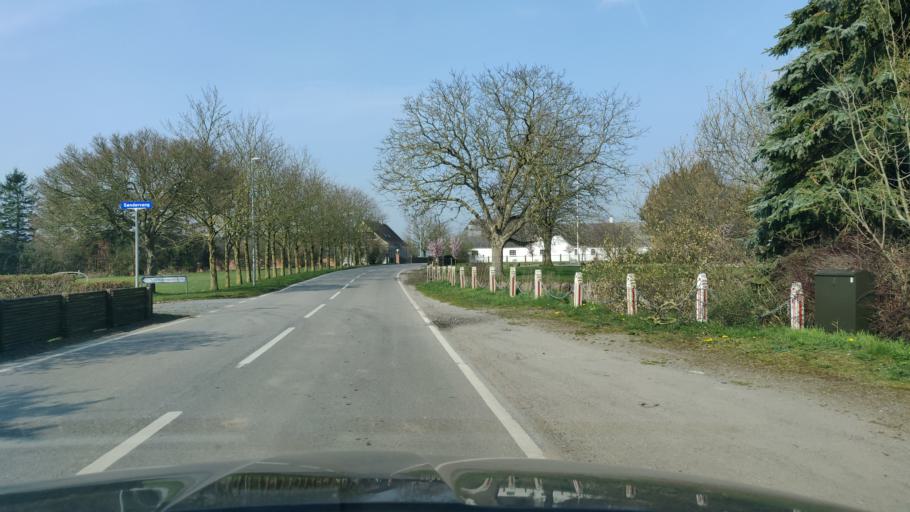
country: DK
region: South Denmark
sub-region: Nordfyns Kommune
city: Sonderso
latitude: 55.5150
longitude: 10.2729
